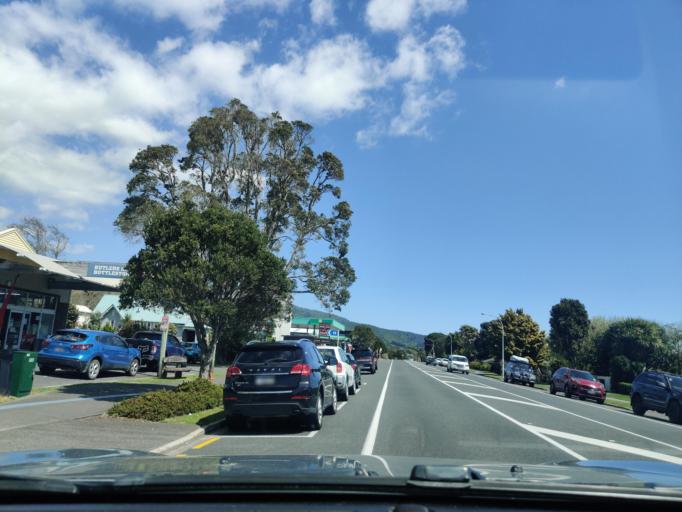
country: NZ
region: Taranaki
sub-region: New Plymouth District
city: New Plymouth
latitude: -39.1159
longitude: 173.9571
